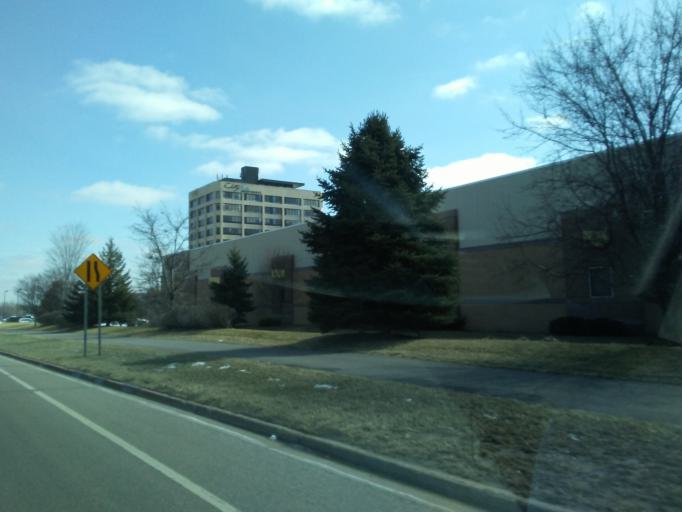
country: US
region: Minnesota
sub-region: Dakota County
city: Eagan
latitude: 44.8334
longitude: -93.1562
